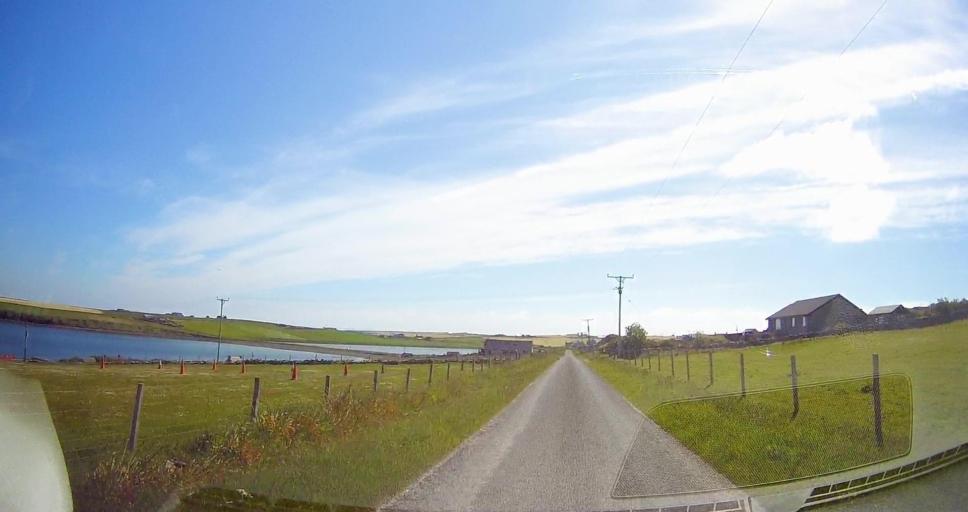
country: GB
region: Scotland
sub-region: Orkney Islands
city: Kirkwall
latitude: 58.8556
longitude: -2.9290
